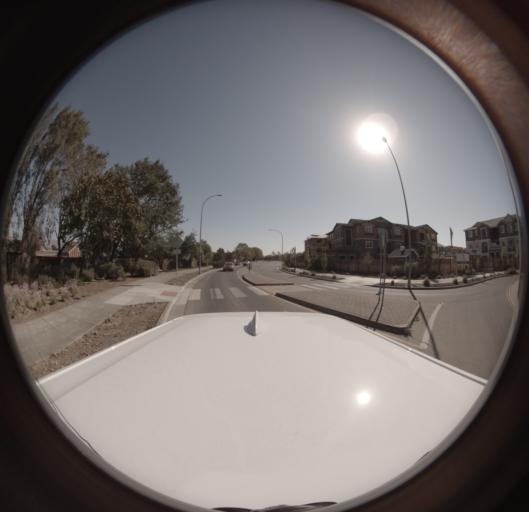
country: US
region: California
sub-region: Sonoma County
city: Penngrove
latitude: 38.2690
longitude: -122.6545
